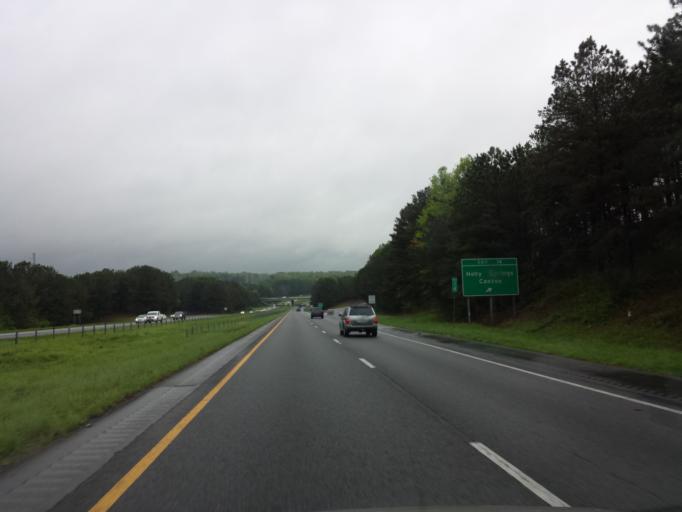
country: US
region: Georgia
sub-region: Cherokee County
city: Holly Springs
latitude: 34.1830
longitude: -84.5066
